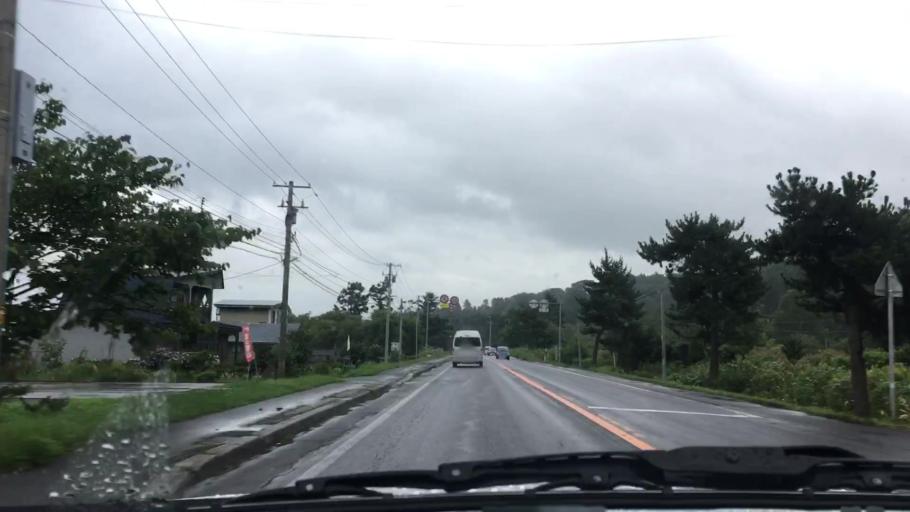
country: JP
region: Hokkaido
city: Nanae
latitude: 42.2256
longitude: 140.3436
